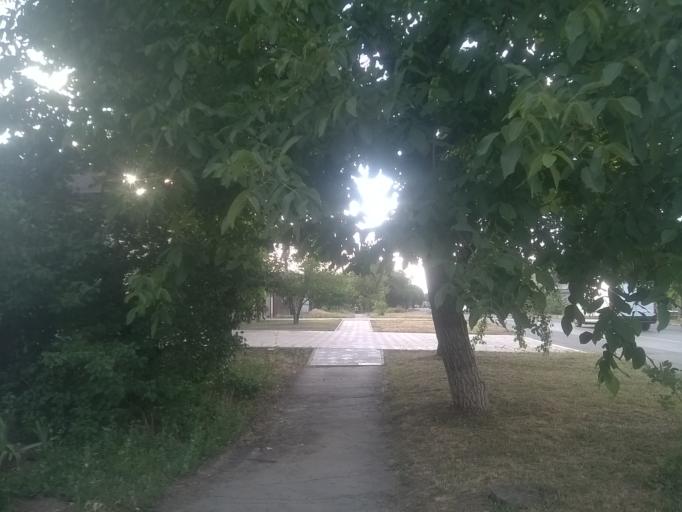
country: RU
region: Rostov
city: Donetsk
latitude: 48.3363
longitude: 39.9564
